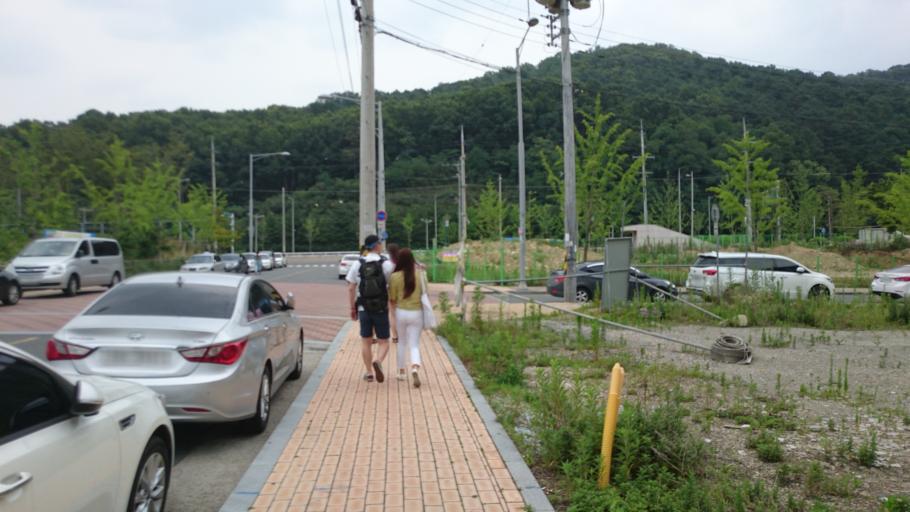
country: KR
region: Daegu
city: Hwawon
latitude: 35.8048
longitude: 128.5195
